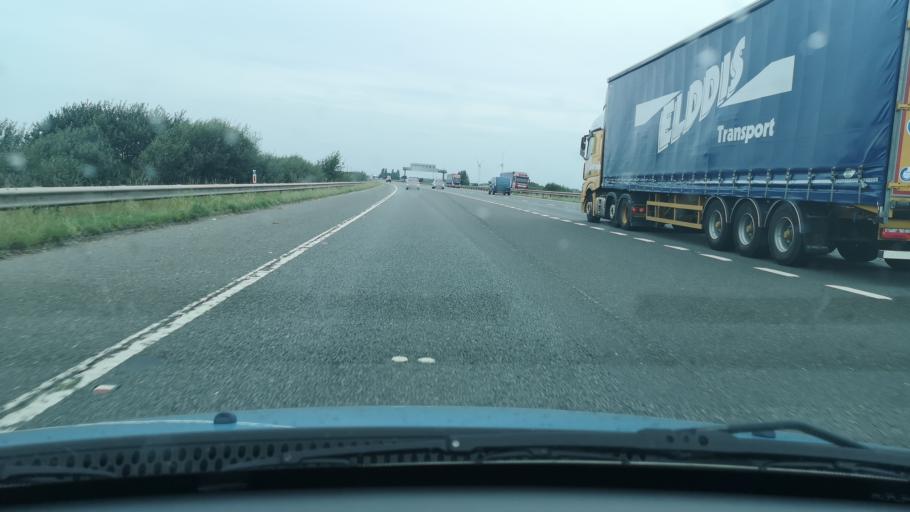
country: GB
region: England
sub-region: North Lincolnshire
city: Gunness
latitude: 53.5581
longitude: -0.7216
